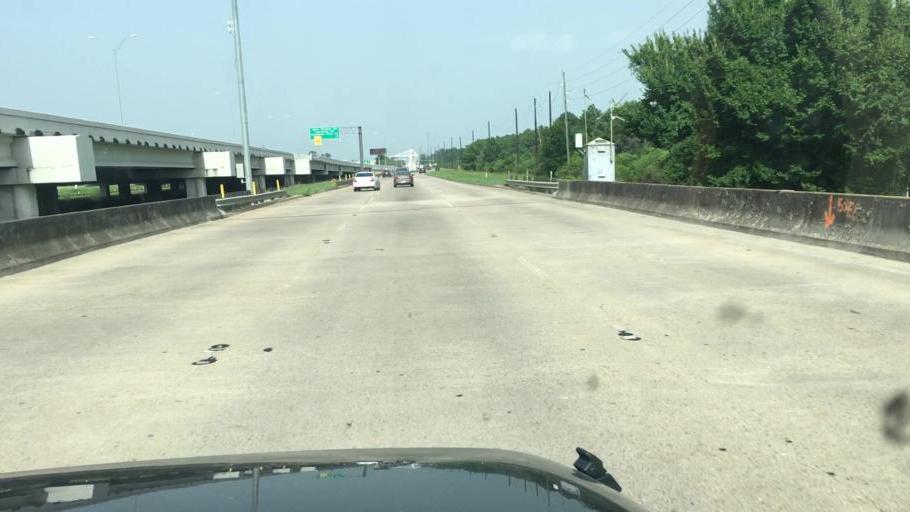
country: US
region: Texas
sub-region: Harris County
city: Humble
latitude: 29.9337
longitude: -95.2339
